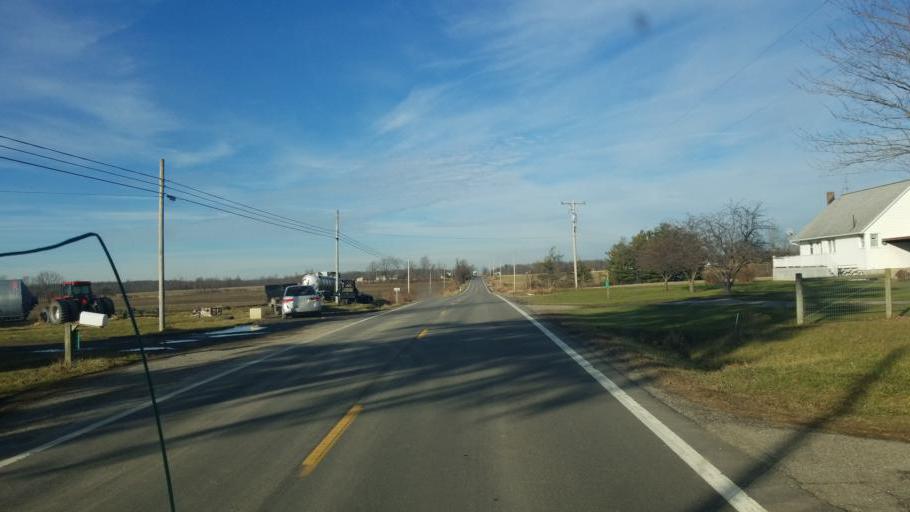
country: US
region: Ohio
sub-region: Ashtabula County
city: Andover
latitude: 41.5399
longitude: -80.6662
